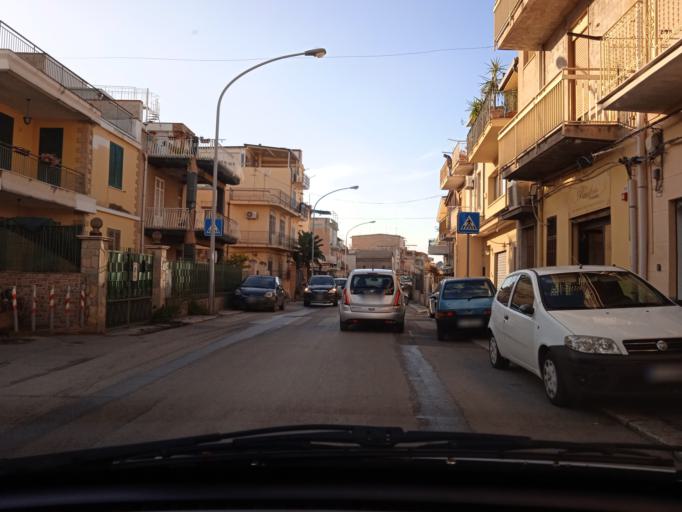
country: IT
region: Sicily
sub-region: Palermo
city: Ciaculli
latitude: 38.0885
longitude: 13.4200
